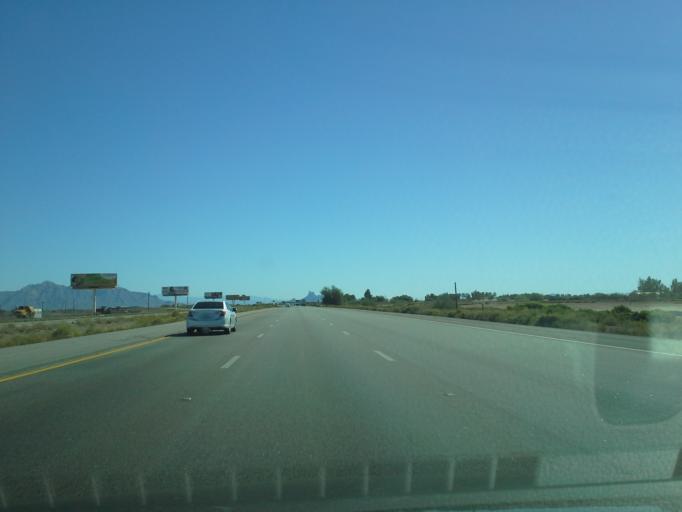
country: US
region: Arizona
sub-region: Pinal County
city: Arizona City
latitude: 32.7736
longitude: -111.6137
